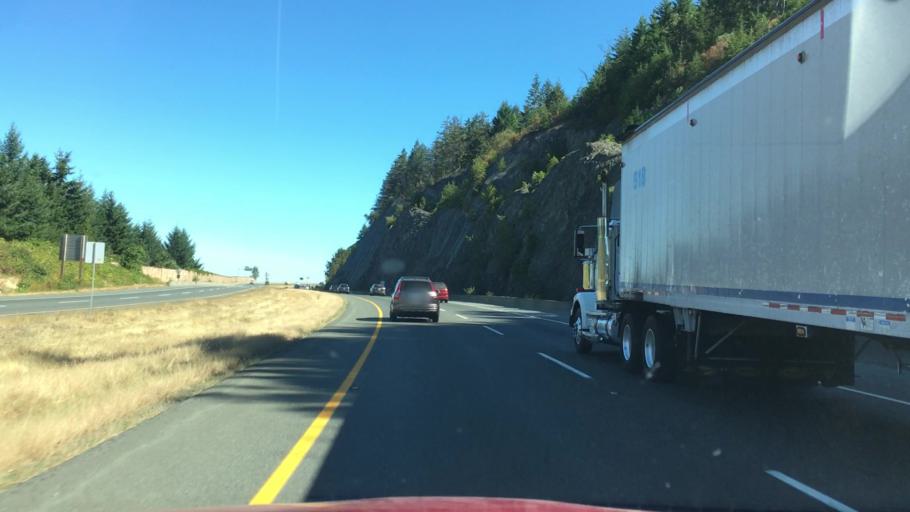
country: CA
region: British Columbia
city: Nanaimo
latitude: 49.1651
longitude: -123.9793
